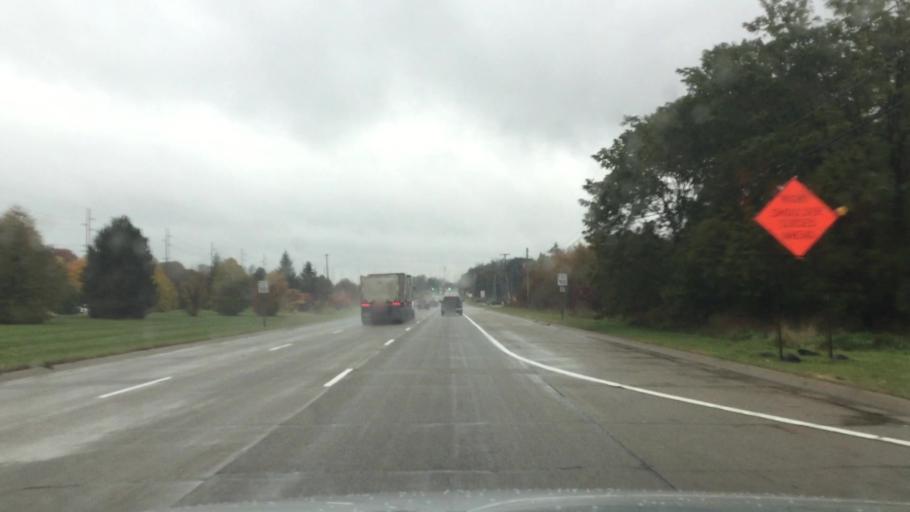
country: US
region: Michigan
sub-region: Macomb County
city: Mount Clemens
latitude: 42.6300
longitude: -82.8793
